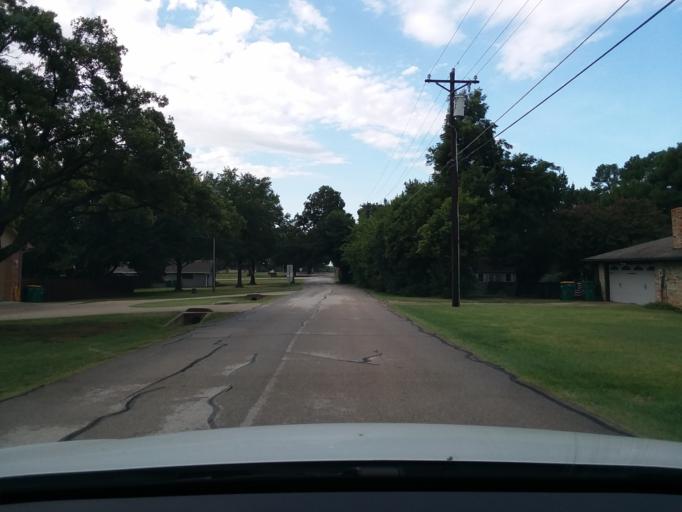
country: US
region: Texas
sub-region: Denton County
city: Double Oak
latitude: 33.0639
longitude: -97.0968
